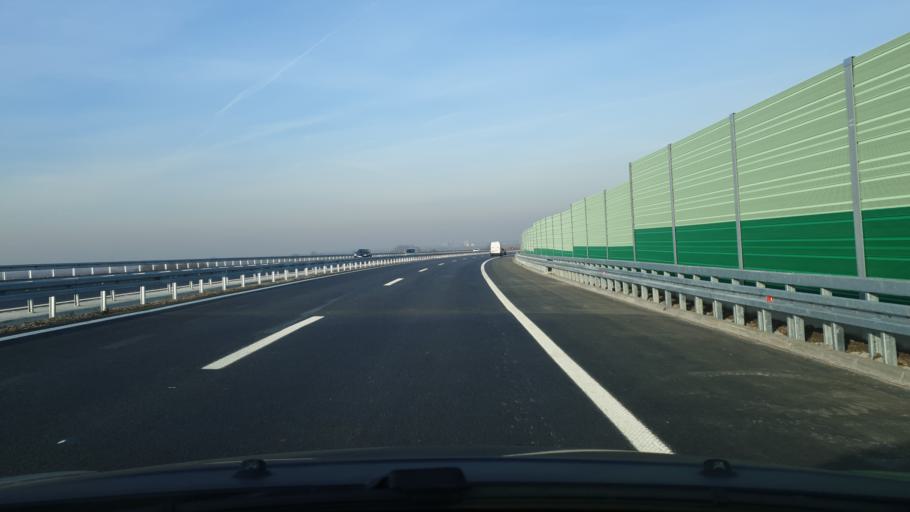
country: RS
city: Boljevci
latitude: 44.7333
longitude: 20.2462
